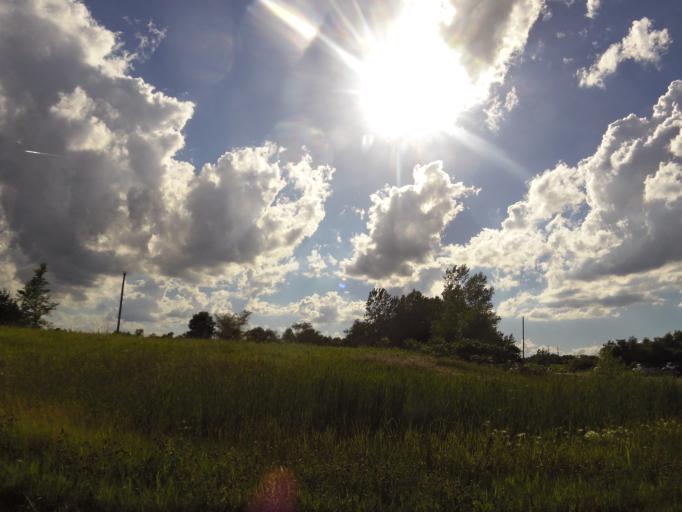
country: US
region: Minnesota
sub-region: Carver County
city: Chaska
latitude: 44.8066
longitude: -93.6442
